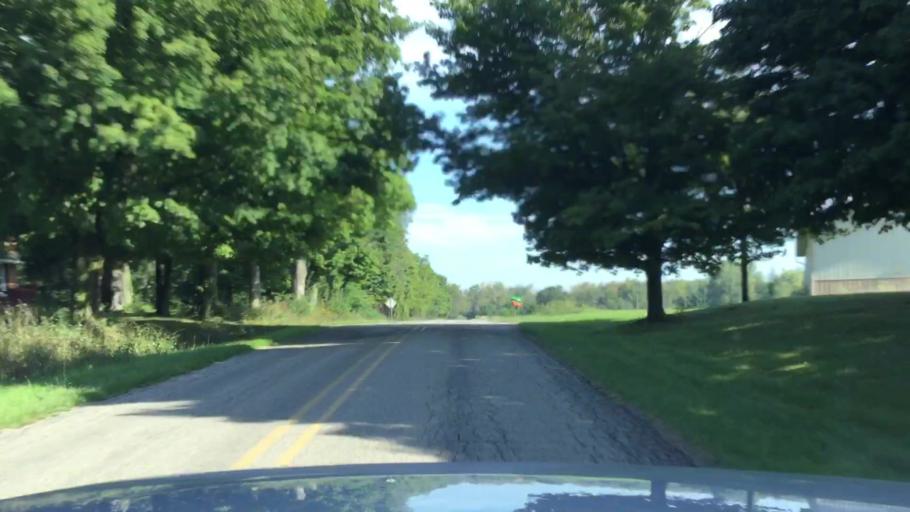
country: US
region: Michigan
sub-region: Lenawee County
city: Hudson
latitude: 41.8995
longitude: -84.4204
